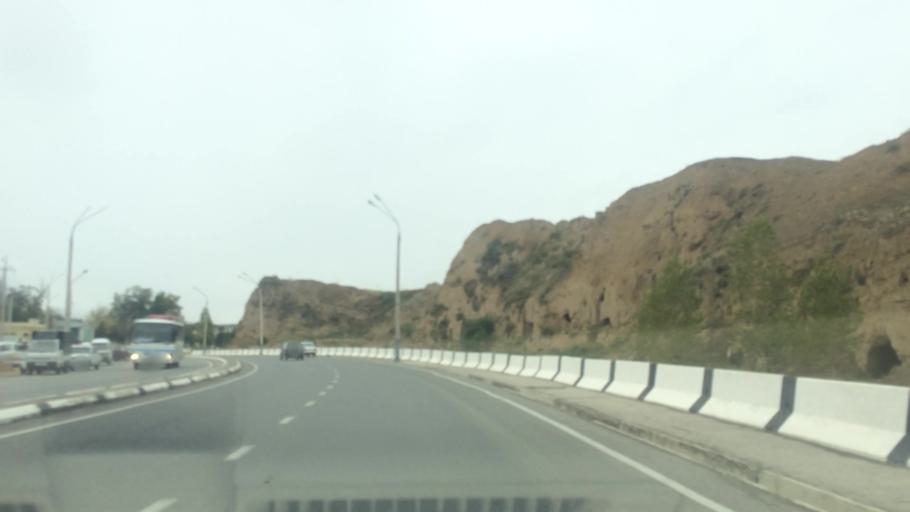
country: UZ
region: Samarqand
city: Samarqand
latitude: 39.6667
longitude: 66.9941
